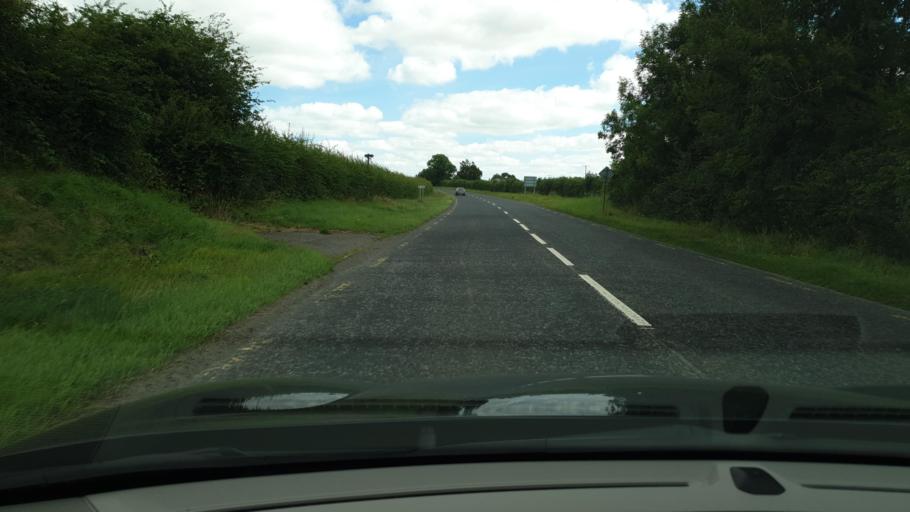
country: IE
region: Leinster
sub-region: An Mhi
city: Newtown Trim
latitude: 53.5361
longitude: -6.7080
